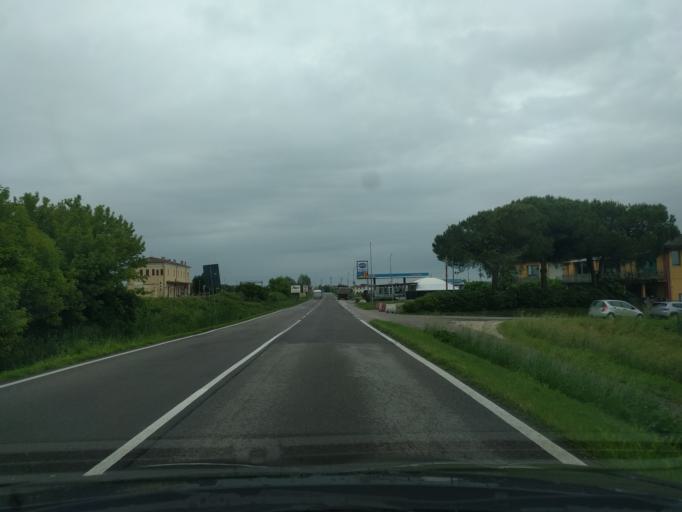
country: IT
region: Veneto
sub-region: Provincia di Rovigo
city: Loreo
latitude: 45.0595
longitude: 12.1895
